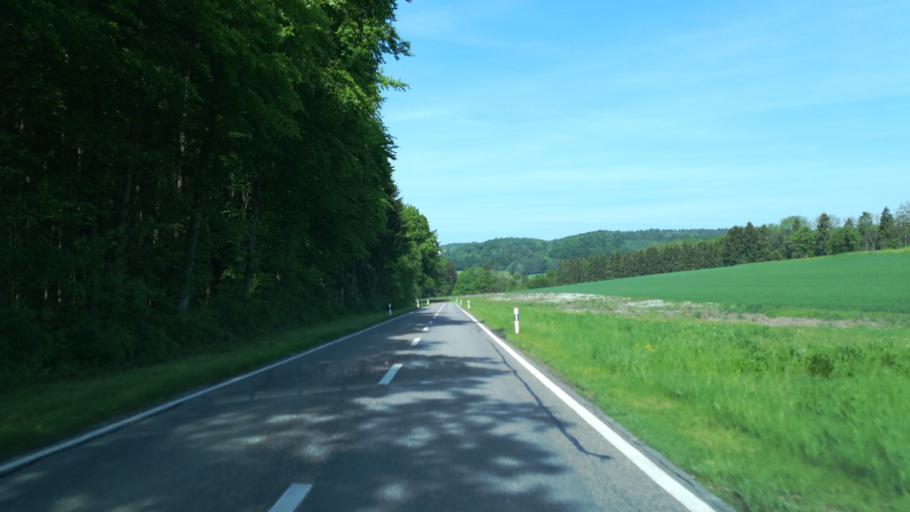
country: CH
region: Thurgau
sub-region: Frauenfeld District
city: Pfyn
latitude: 47.6091
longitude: 8.9336
